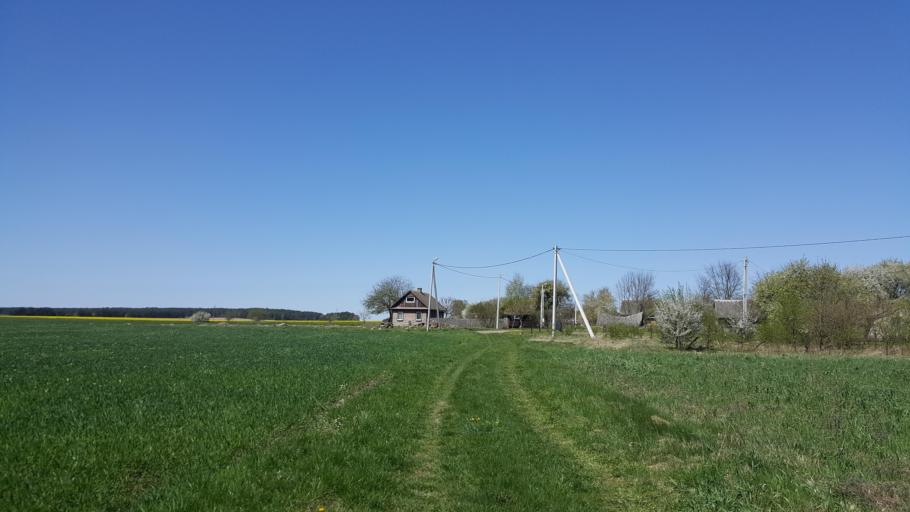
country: BY
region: Brest
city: Charnawchytsy
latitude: 52.3187
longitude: 23.7087
